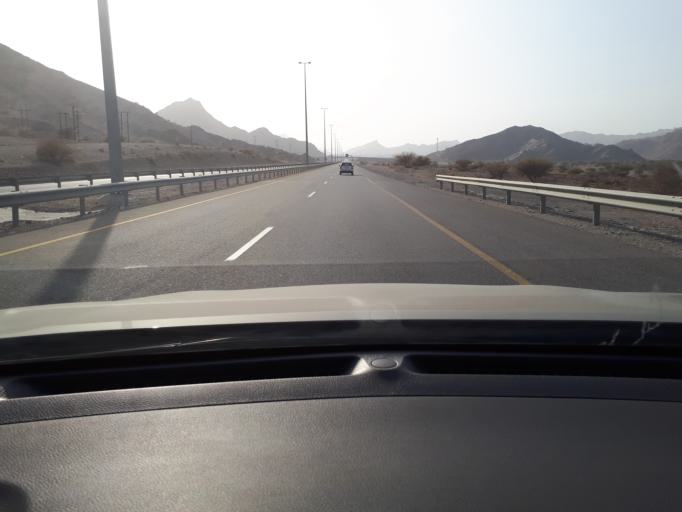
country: OM
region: Muhafazat Masqat
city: Muscat
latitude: 23.3526
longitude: 58.6855
